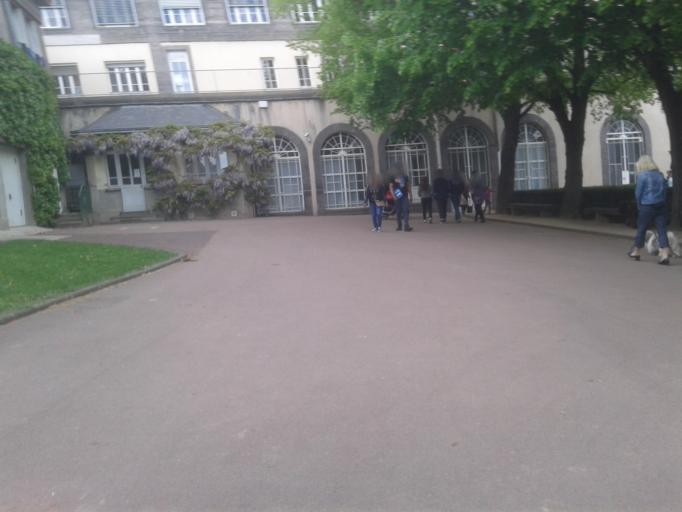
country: FR
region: Auvergne
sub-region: Departement du Puy-de-Dome
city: Clermont-Ferrand
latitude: 45.7721
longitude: 3.0873
